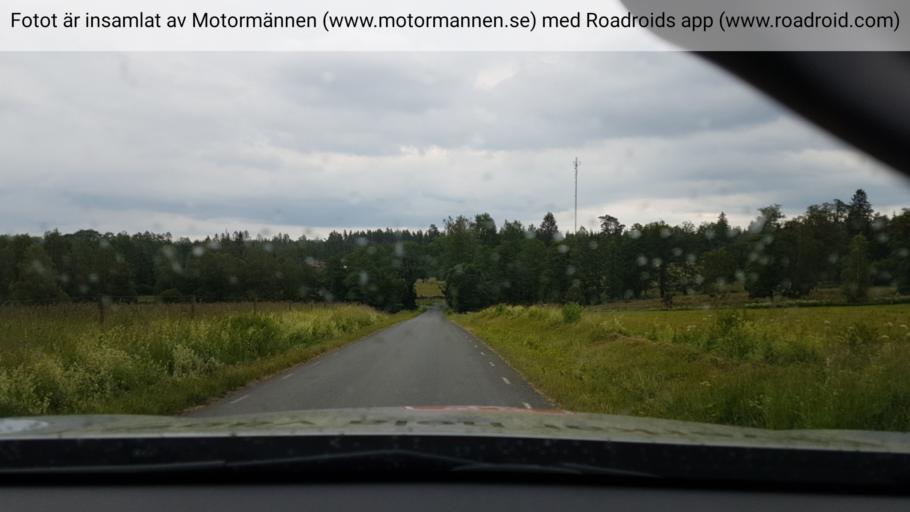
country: SE
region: Joenkoeping
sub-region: Mullsjo Kommun
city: Mullsjoe
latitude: 57.9764
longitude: 13.7582
